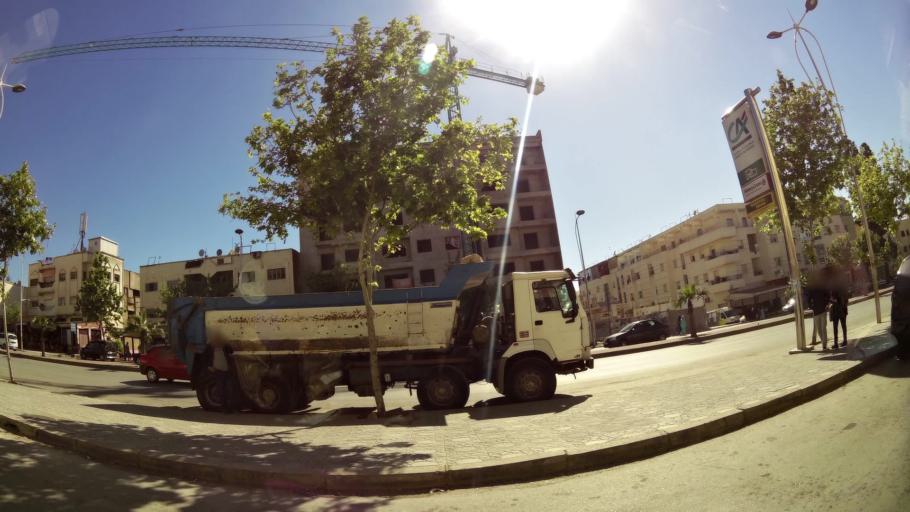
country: MA
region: Fes-Boulemane
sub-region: Fes
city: Fes
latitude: 34.0109
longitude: -4.9801
